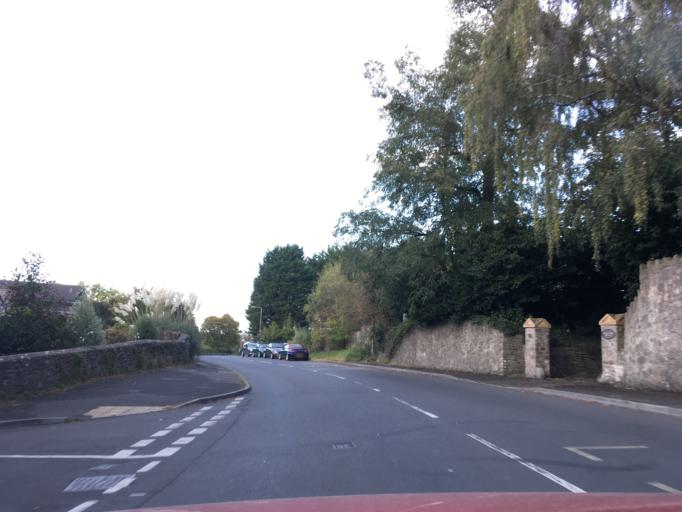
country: GB
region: England
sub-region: North Somerset
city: Easton-in-Gordano
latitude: 51.4764
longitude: -2.6994
